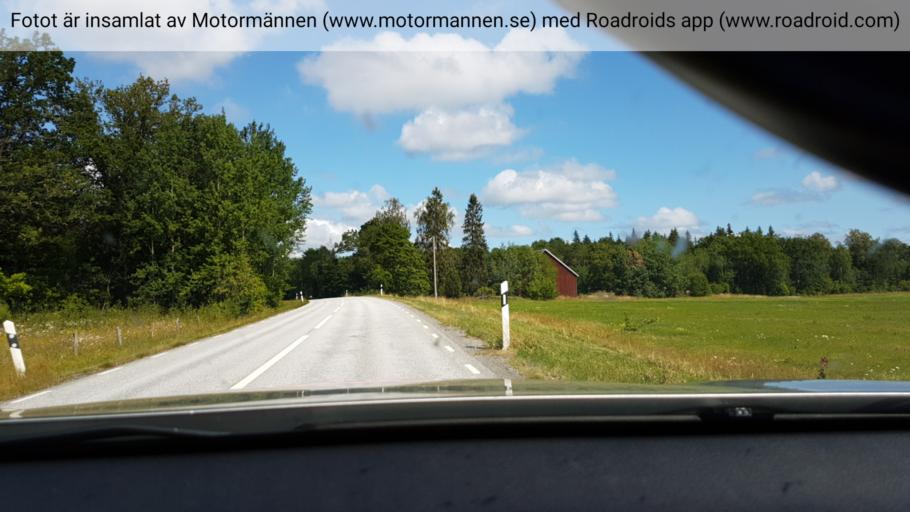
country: SE
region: Stockholm
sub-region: Norrtalje Kommun
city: Norrtalje
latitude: 59.9219
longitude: 18.7100
